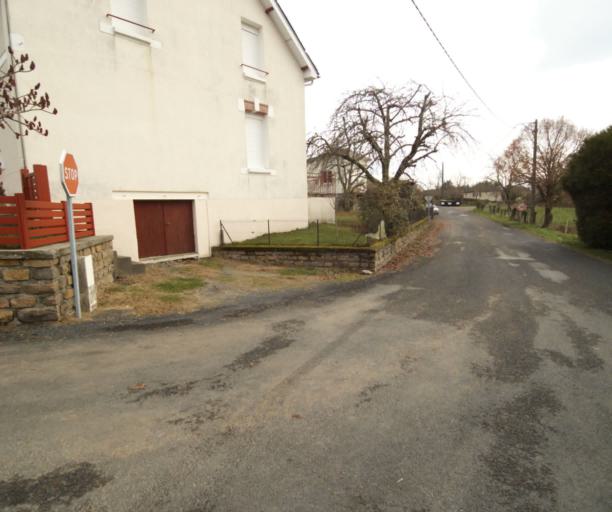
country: FR
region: Limousin
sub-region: Departement de la Correze
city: Chameyrat
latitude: 45.2649
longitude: 1.7215
